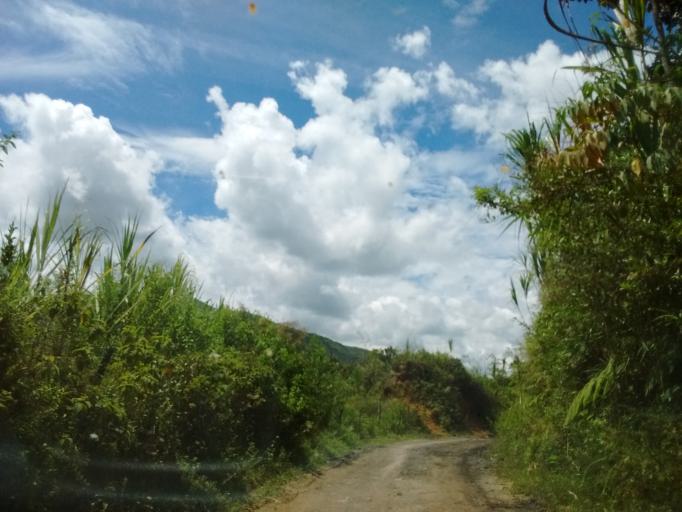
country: CO
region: Cauca
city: Villa Rica
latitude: 2.6520
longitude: -76.7702
